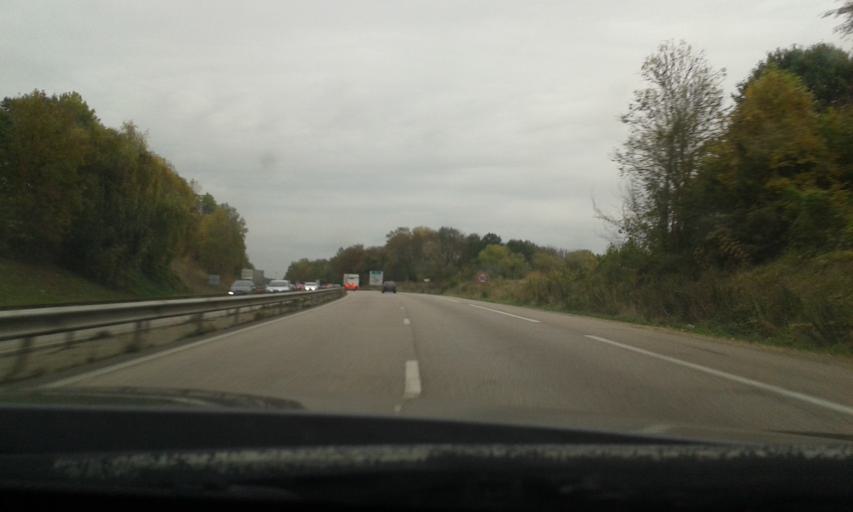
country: FR
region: Haute-Normandie
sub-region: Departement de la Seine-Maritime
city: Oissel
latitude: 49.3423
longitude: 1.0752
